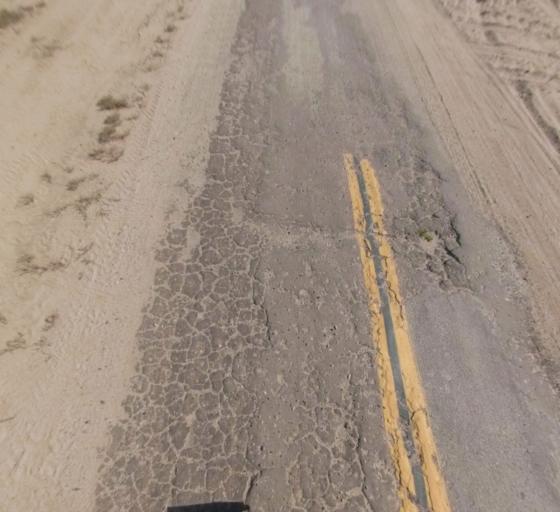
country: US
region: California
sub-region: Fresno County
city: Biola
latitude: 36.8306
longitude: -120.0156
